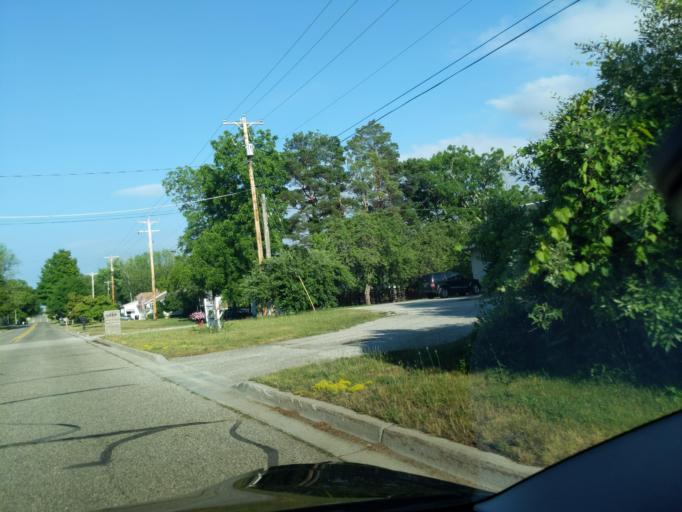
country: US
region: Michigan
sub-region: Muskegon County
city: Whitehall
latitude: 43.4034
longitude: -86.3321
